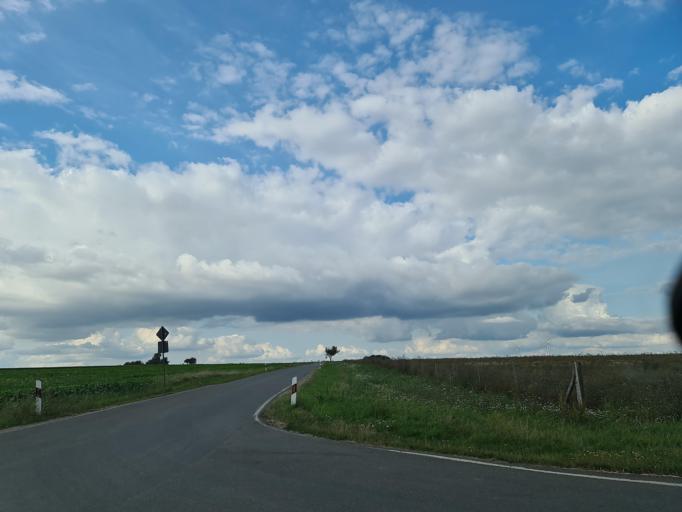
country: DE
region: Thuringia
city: Walpernhain
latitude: 51.0301
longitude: 11.9713
